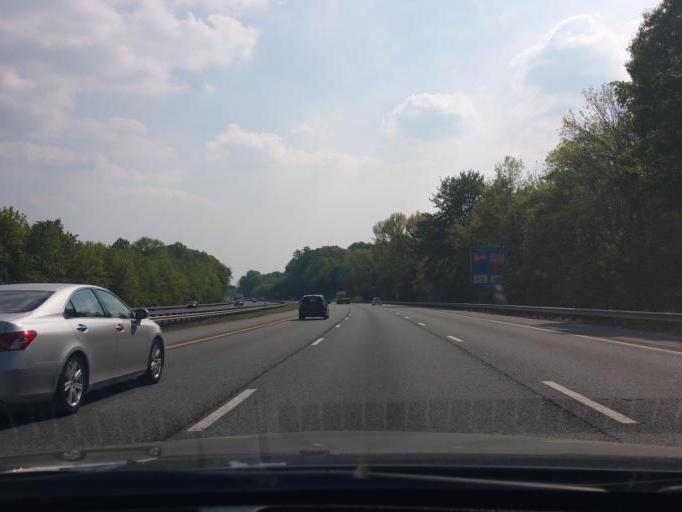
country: US
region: Maryland
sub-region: Harford County
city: Aberdeen
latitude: 39.5460
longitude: -76.1678
